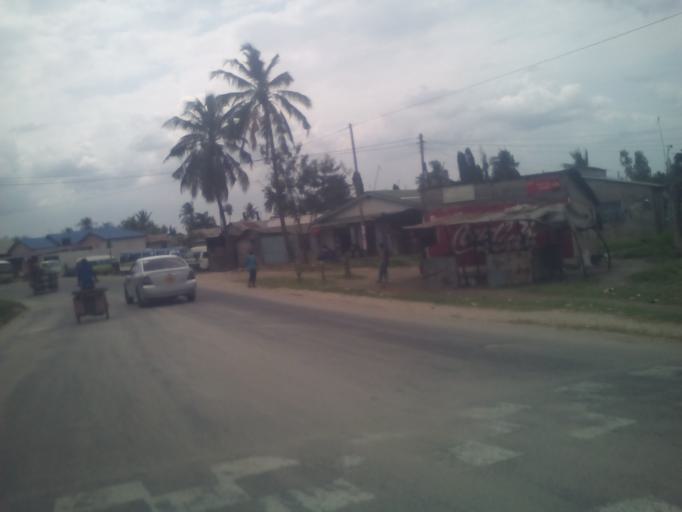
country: TZ
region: Dar es Salaam
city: Dar es Salaam
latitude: -6.8705
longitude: 39.2230
